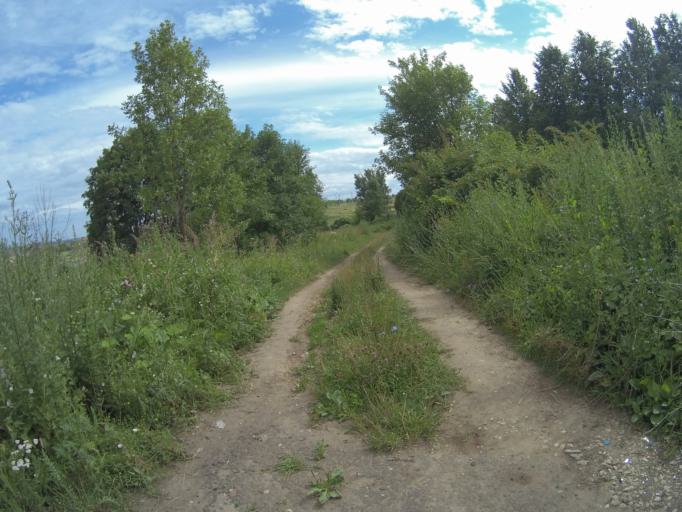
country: RU
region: Vladimir
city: Bogolyubovo
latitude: 56.2108
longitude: 40.5236
